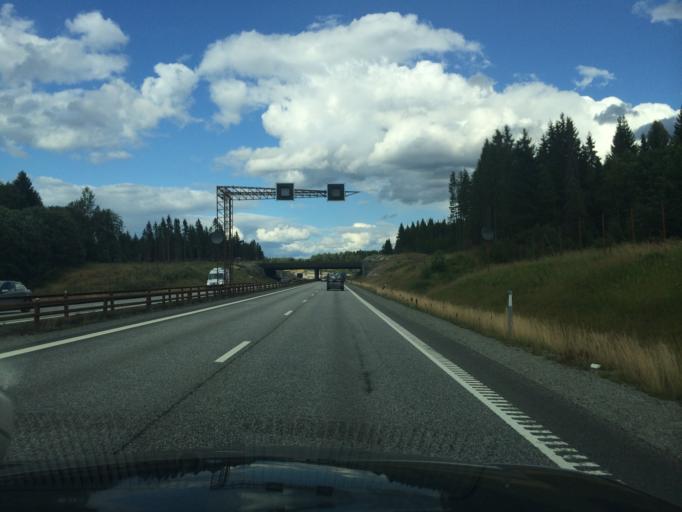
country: NO
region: Akershus
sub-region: Eidsvoll
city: Raholt
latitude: 60.3248
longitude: 11.1789
